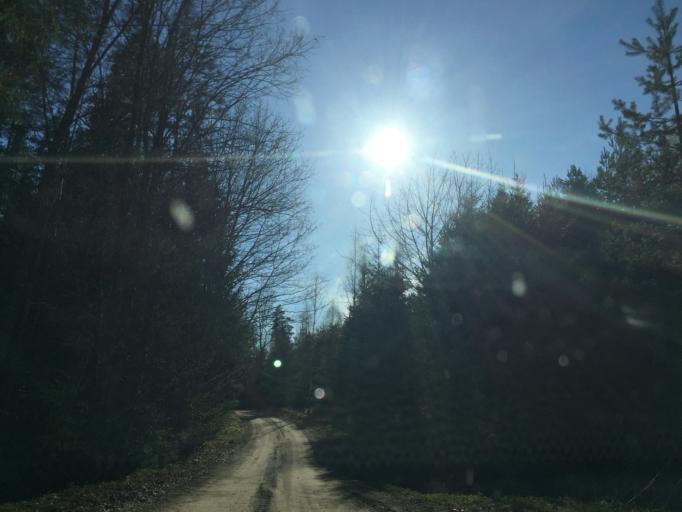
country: EE
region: Valgamaa
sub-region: Valga linn
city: Valga
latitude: 57.7733
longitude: 26.2237
